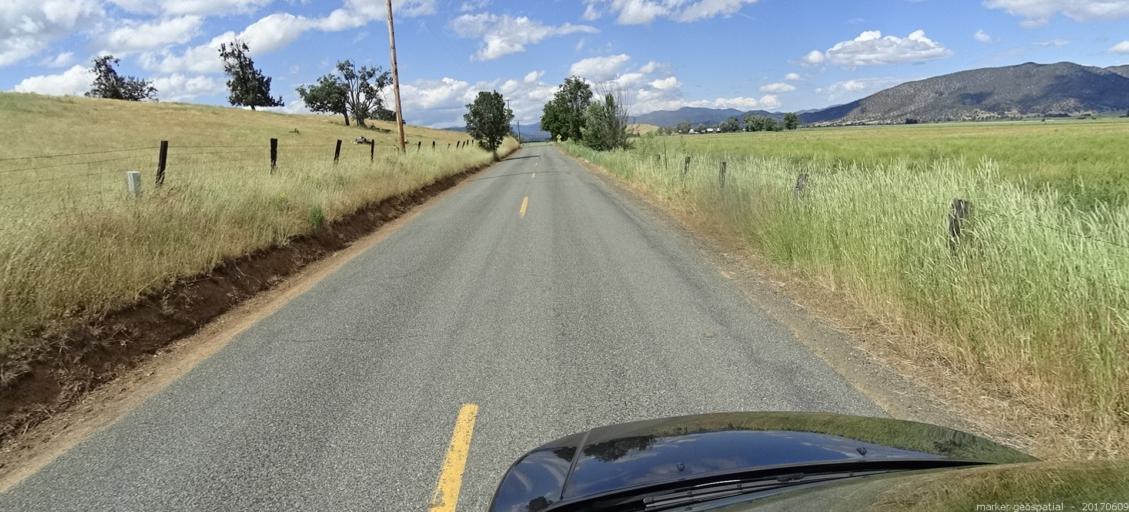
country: US
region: California
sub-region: Siskiyou County
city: Yreka
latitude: 41.4822
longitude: -122.8768
